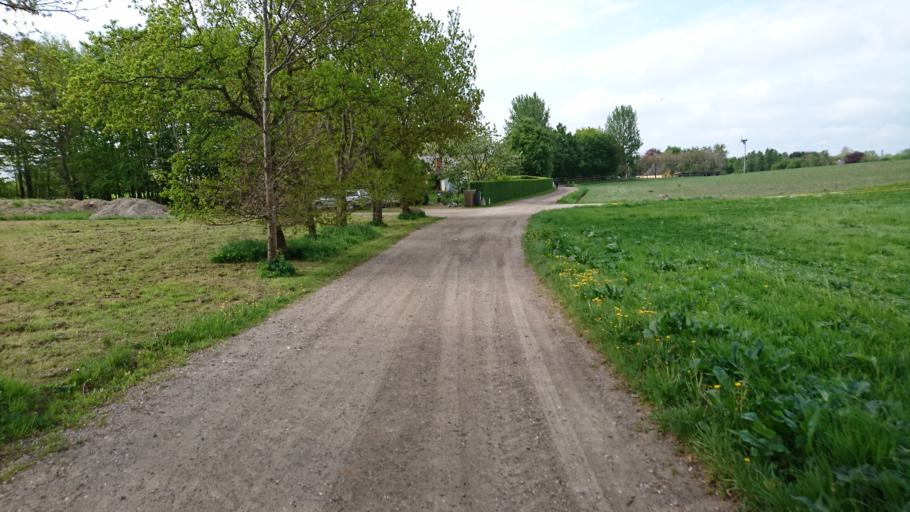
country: DK
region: Capital Region
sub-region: Ballerup Kommune
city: Malov
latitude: 55.7377
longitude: 12.3260
